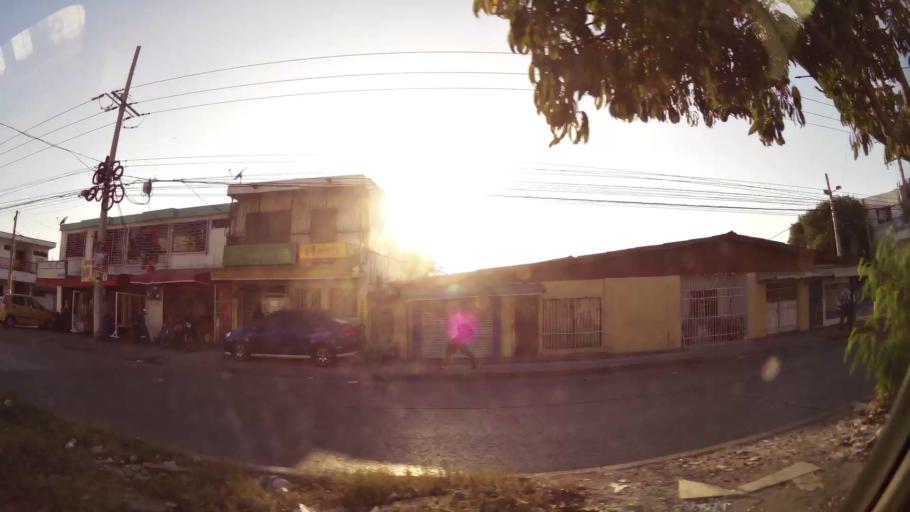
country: CO
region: Bolivar
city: Cartagena
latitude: 10.4097
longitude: -75.5218
